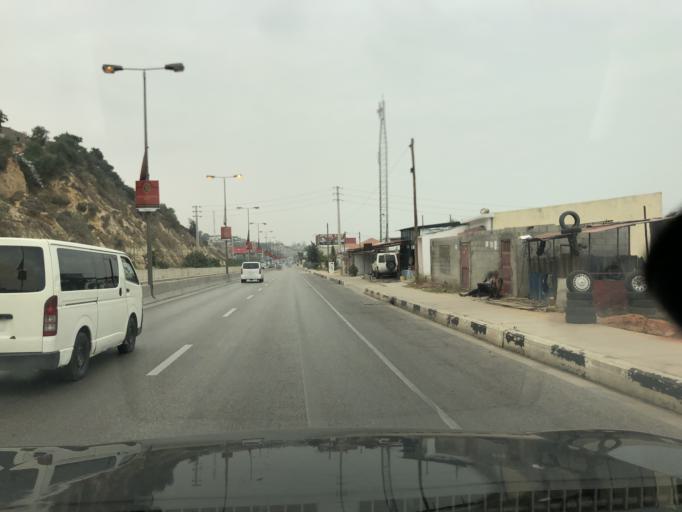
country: AO
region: Luanda
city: Luanda
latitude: -8.8668
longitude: 13.1996
